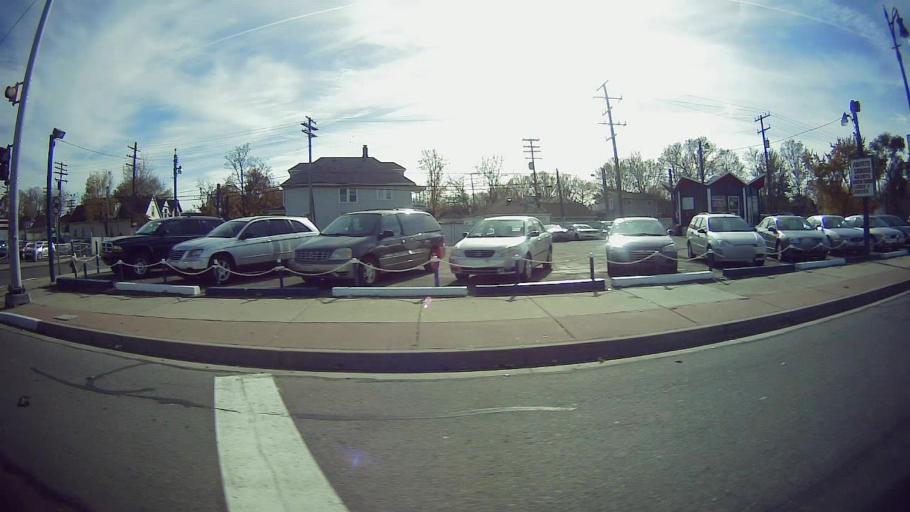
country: US
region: Michigan
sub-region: Wayne County
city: Dearborn
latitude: 42.3299
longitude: -83.1475
